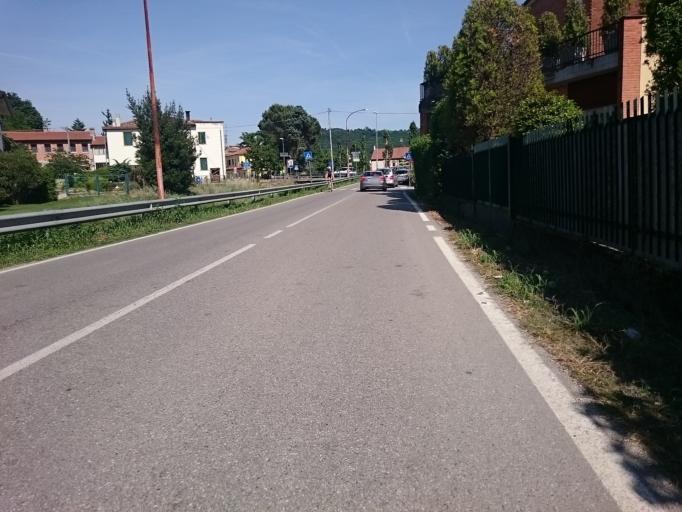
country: IT
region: Veneto
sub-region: Provincia di Padova
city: Treponti
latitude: 45.3663
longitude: 11.7063
